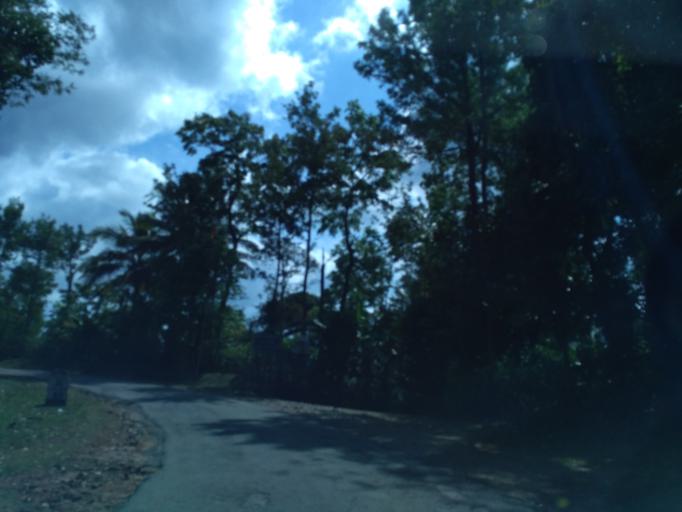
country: IN
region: Karnataka
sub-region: Kodagu
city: Madikeri
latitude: 12.3996
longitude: 75.7110
